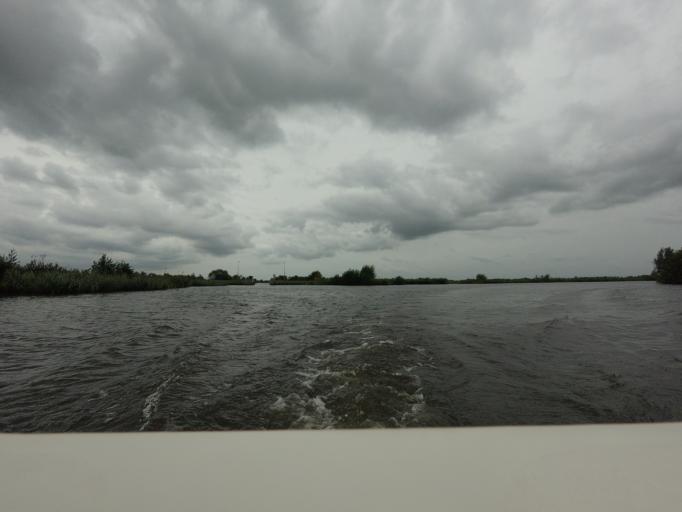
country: NL
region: Friesland
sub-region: Gemeente Boarnsterhim
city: Aldeboarn
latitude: 53.0945
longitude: 5.9226
